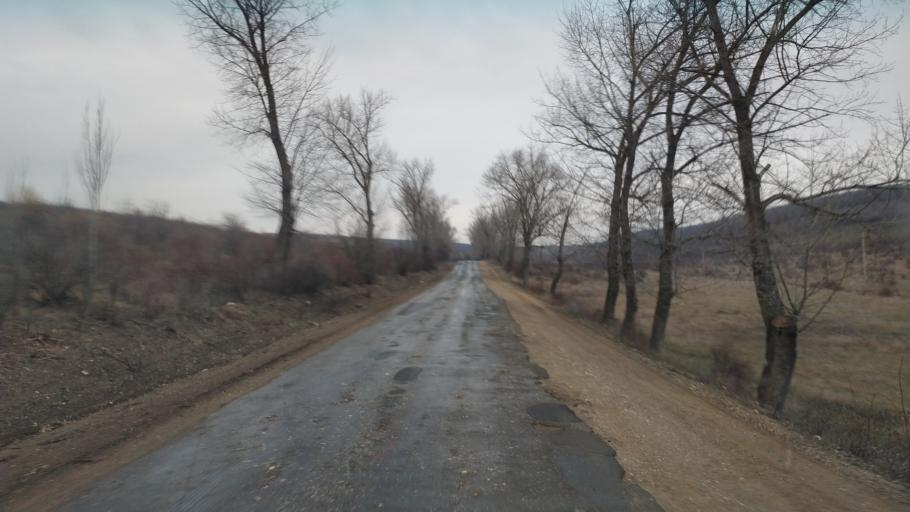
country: MD
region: Chisinau
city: Singera
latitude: 46.8432
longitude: 28.9822
